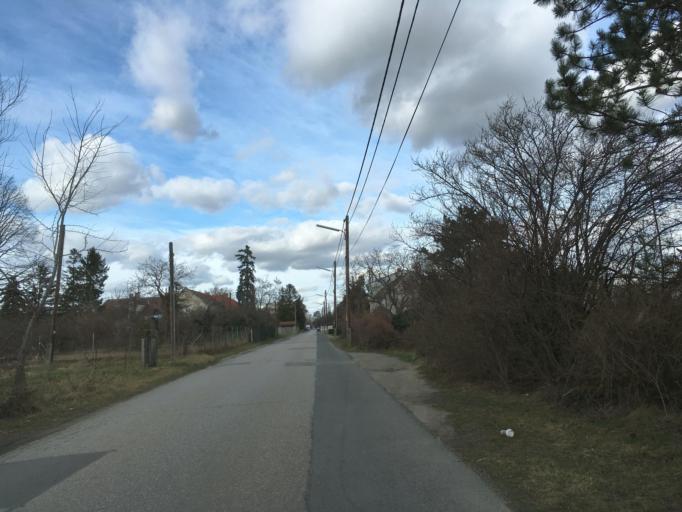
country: AT
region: Lower Austria
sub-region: Politischer Bezirk Ganserndorf
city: Gross-Enzersdorf
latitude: 48.2116
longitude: 16.5036
